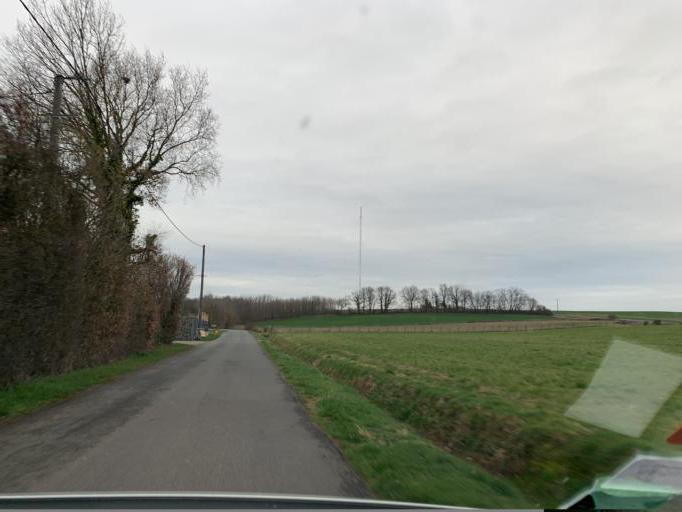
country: FR
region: Rhone-Alpes
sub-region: Departement de l'Ain
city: Mionnay
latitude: 45.8738
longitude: 4.9377
